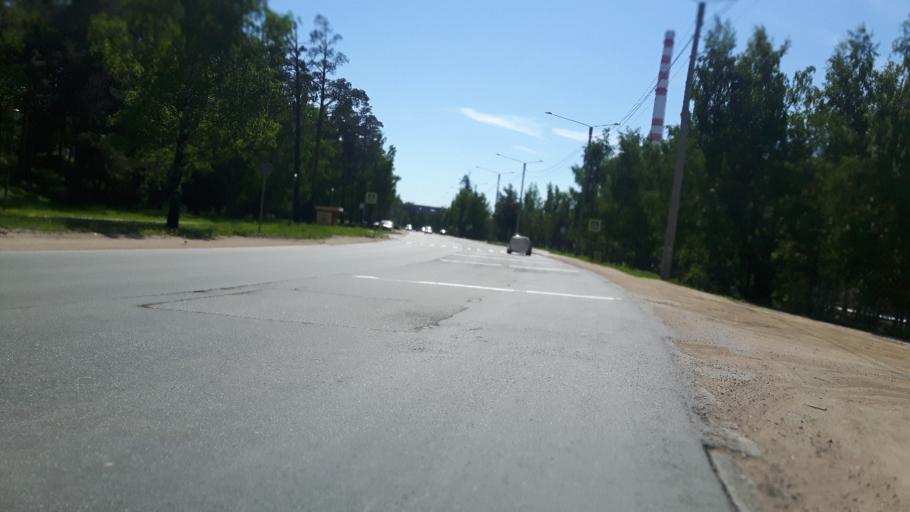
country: RU
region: Leningrad
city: Sosnovyy Bor
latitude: 59.8557
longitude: 29.0560
